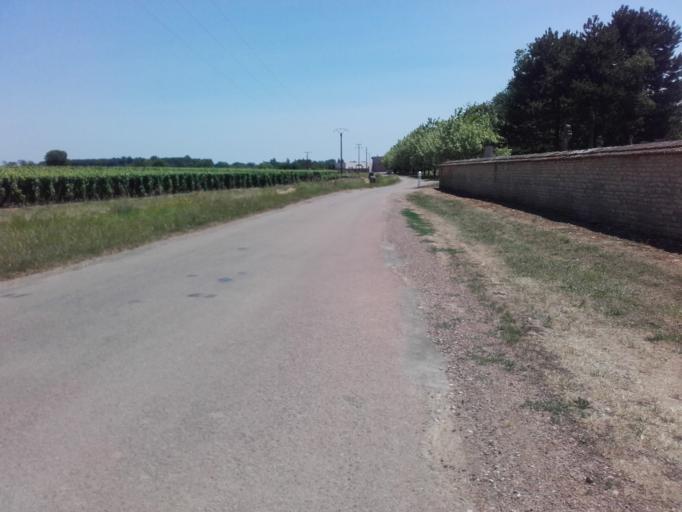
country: FR
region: Bourgogne
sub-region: Departement de la Cote-d'Or
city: Corpeau
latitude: 46.9499
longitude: 4.7535
